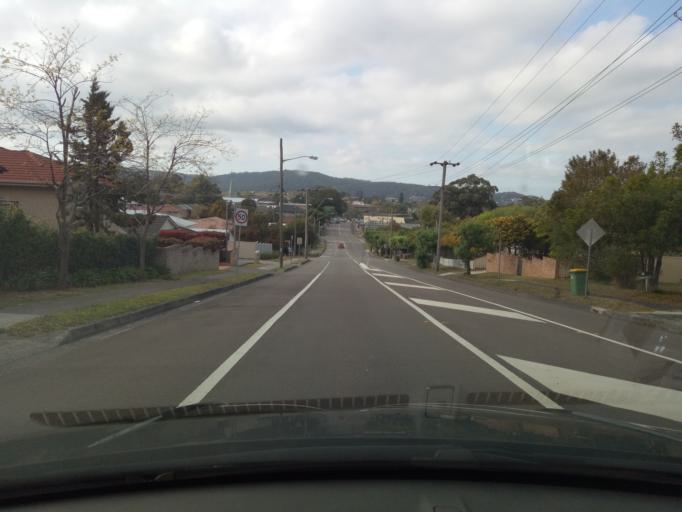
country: AU
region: New South Wales
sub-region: Gosford Shire
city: East Gosford
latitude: -33.4343
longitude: 151.3491
